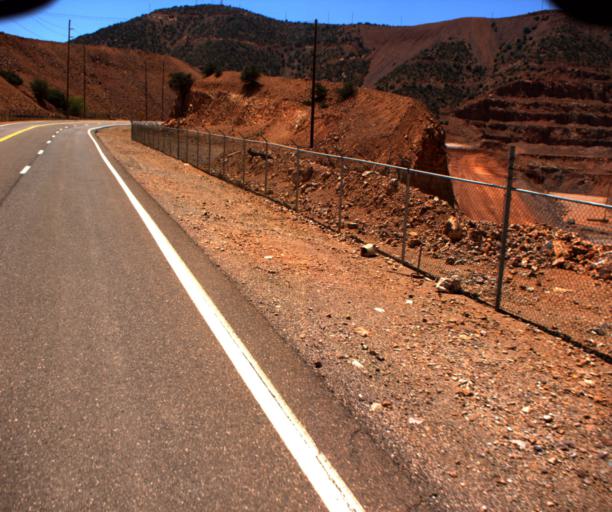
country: US
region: Arizona
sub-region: Greenlee County
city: Morenci
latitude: 33.1045
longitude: -109.3775
